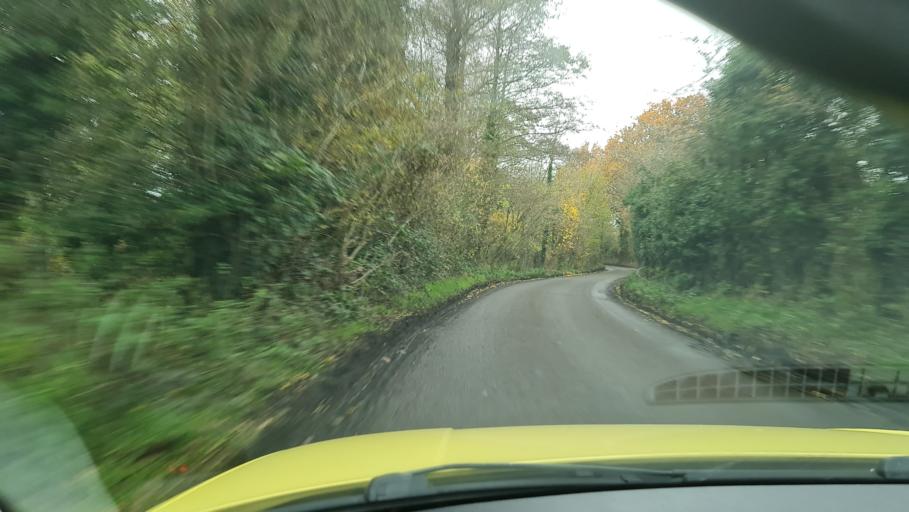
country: GB
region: England
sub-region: Hampshire
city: Yateley
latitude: 51.3547
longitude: -0.8249
